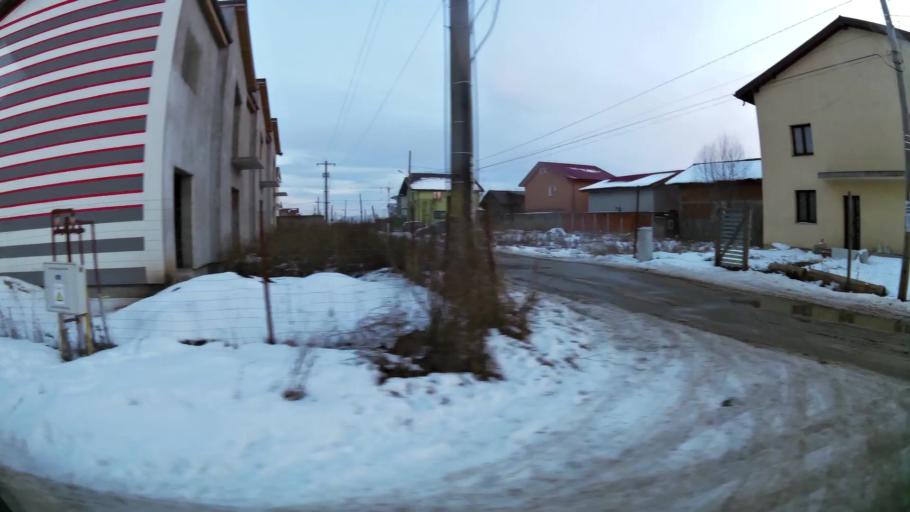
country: RO
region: Ilfov
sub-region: Comuna Magurele
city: Magurele
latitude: 44.3841
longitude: 26.0247
